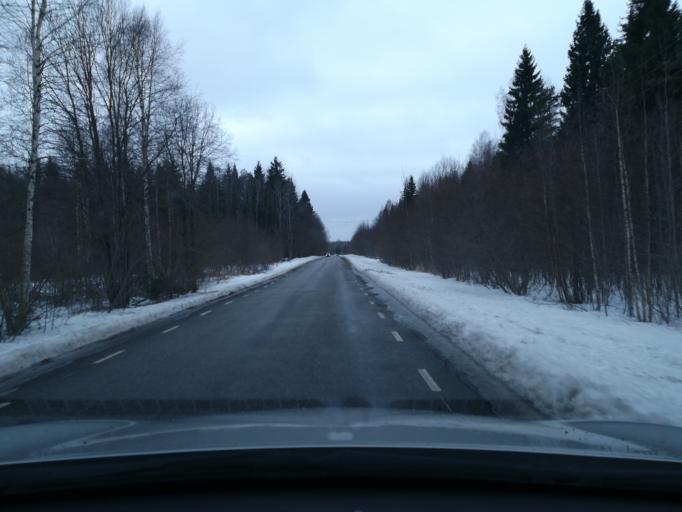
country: EE
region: Harju
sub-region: Nissi vald
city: Turba
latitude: 59.0675
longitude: 24.2517
